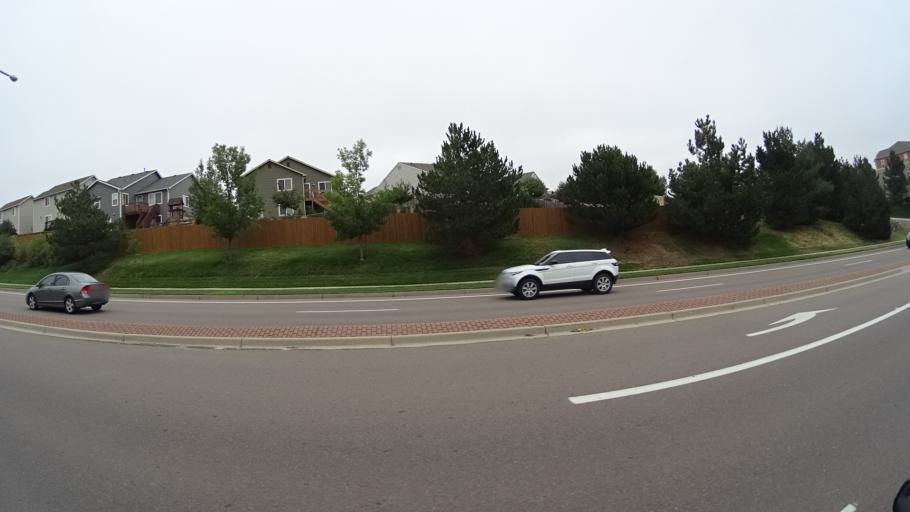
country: US
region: Colorado
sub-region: El Paso County
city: Cimarron Hills
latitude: 38.9122
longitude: -104.7151
